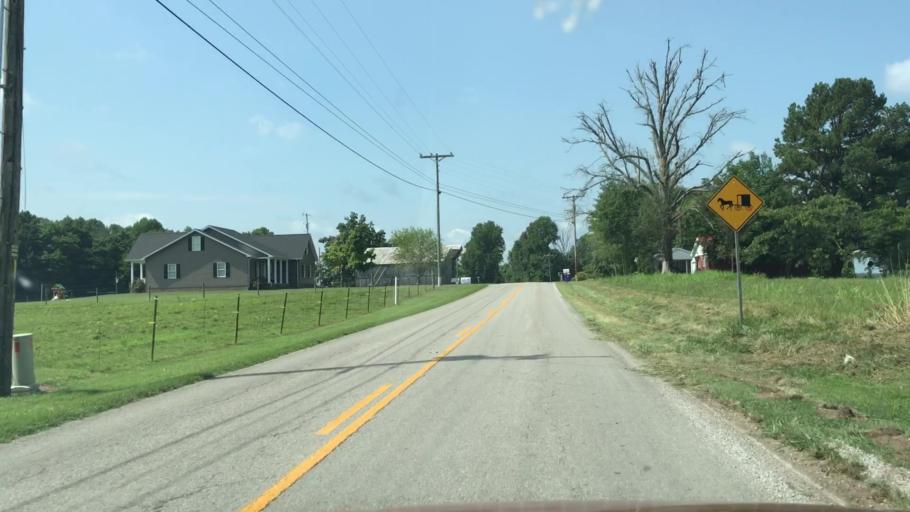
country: US
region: Kentucky
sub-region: Barren County
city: Glasgow
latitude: 36.8827
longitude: -85.8463
